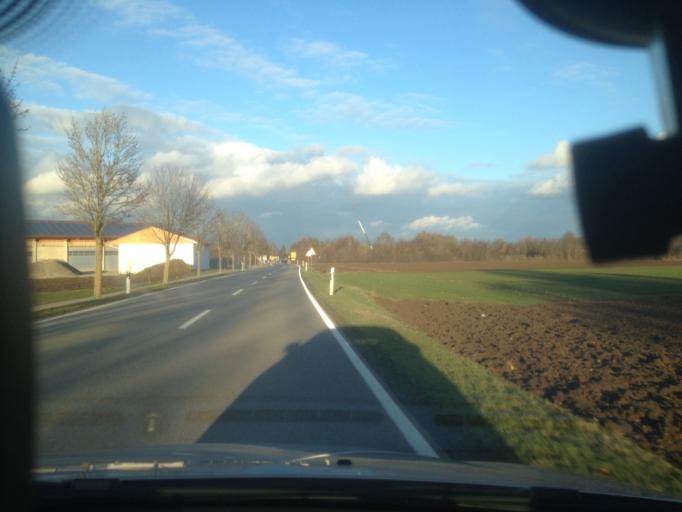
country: DE
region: Bavaria
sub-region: Swabia
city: Merching
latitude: 48.2551
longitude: 10.9736
